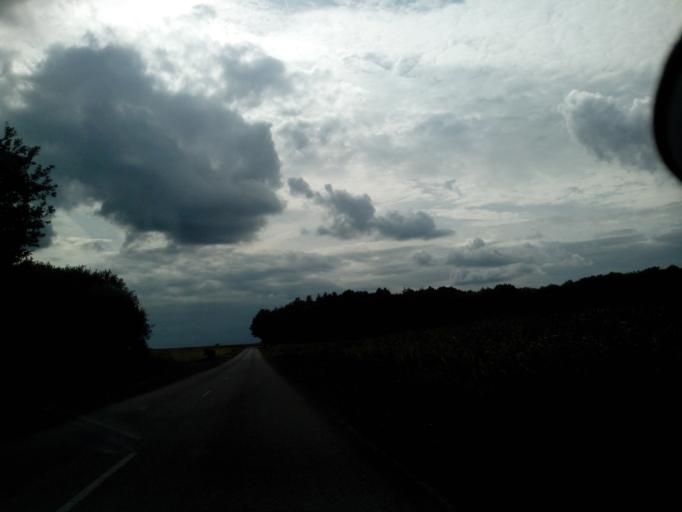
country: FR
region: Brittany
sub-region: Departement du Morbihan
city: Mauron
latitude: 48.1210
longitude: -2.2812
